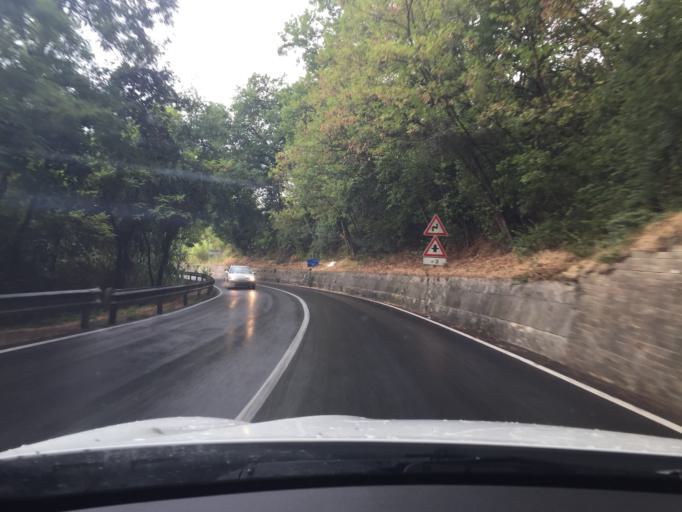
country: IT
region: Umbria
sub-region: Provincia di Perugia
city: San Martino in Campo
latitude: 43.0714
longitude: 12.3985
